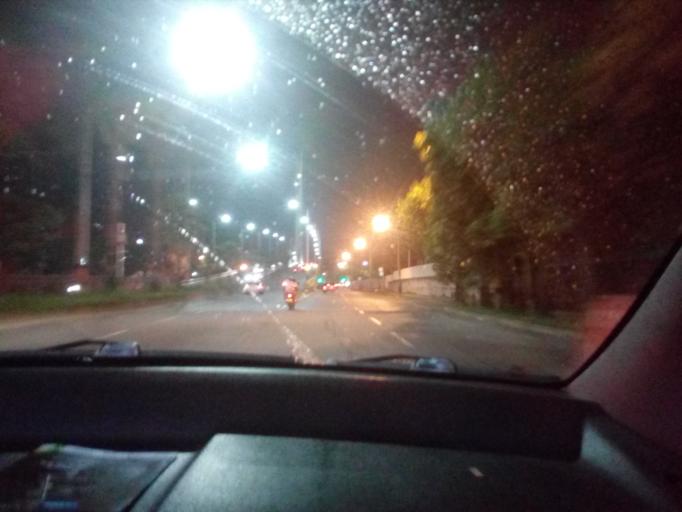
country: CO
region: Antioquia
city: Envigado
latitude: 6.1758
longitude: -75.5909
